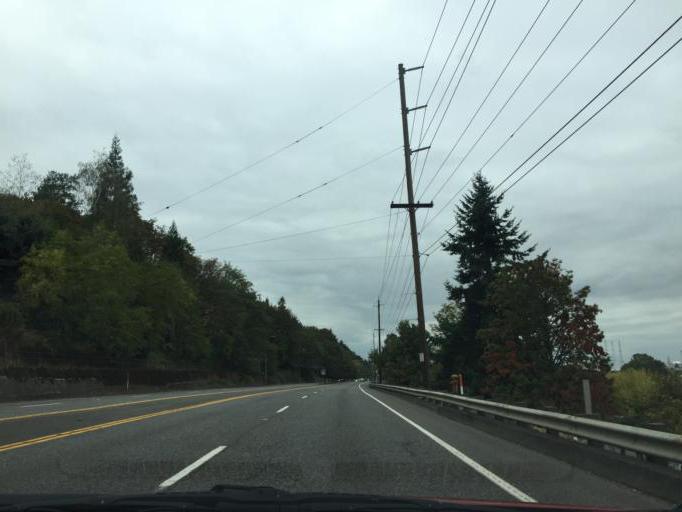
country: US
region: Oregon
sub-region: Washington County
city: Cedar Mill
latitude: 45.5934
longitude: -122.7817
